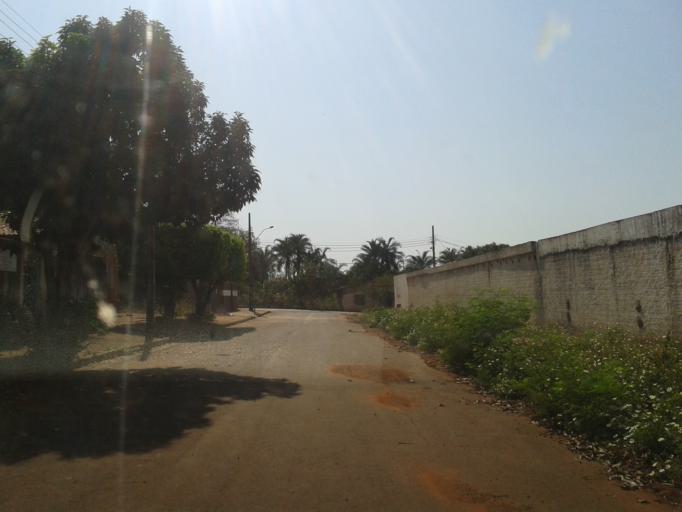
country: BR
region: Minas Gerais
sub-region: Ituiutaba
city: Ituiutaba
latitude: -18.9637
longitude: -49.4804
